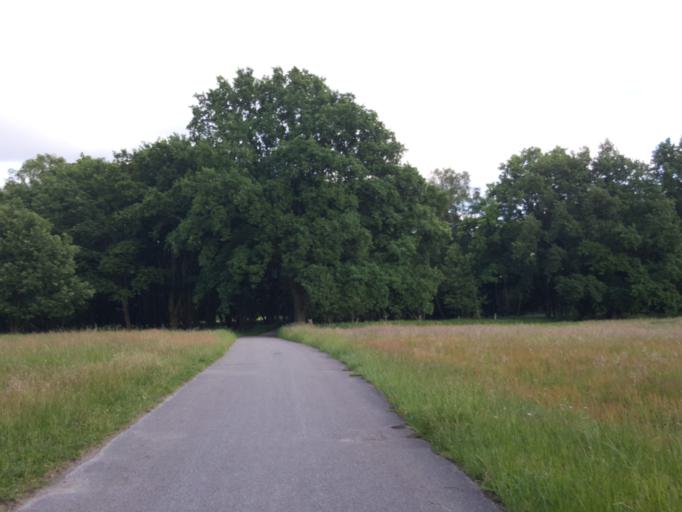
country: DE
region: Schleswig-Holstein
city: Oststeinbek
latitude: 53.5128
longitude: 10.1393
